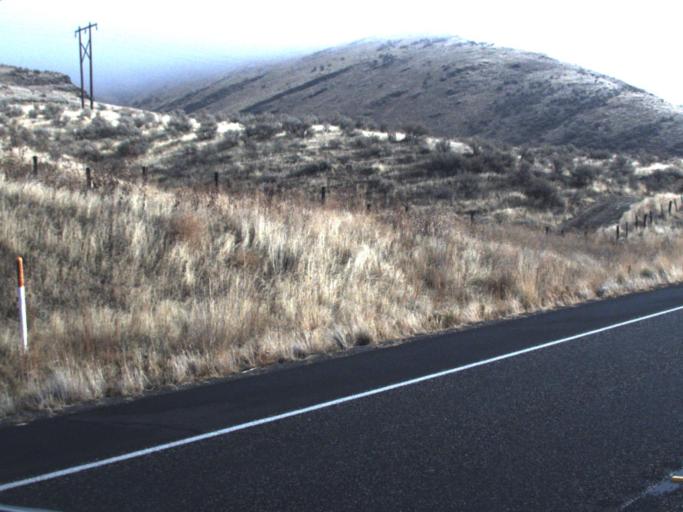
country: US
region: Washington
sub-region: Asotin County
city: Clarkston Heights-Vineland
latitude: 46.4050
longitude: -117.2531
